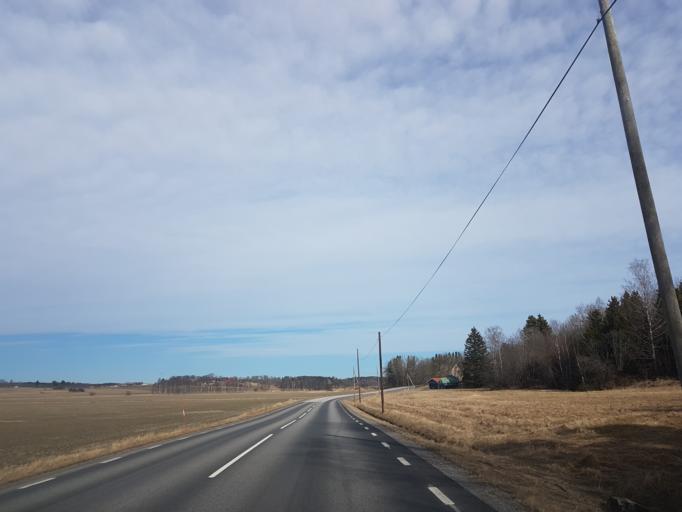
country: SE
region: Stockholm
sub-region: Norrtalje Kommun
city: Rimbo
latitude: 59.7294
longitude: 18.5150
